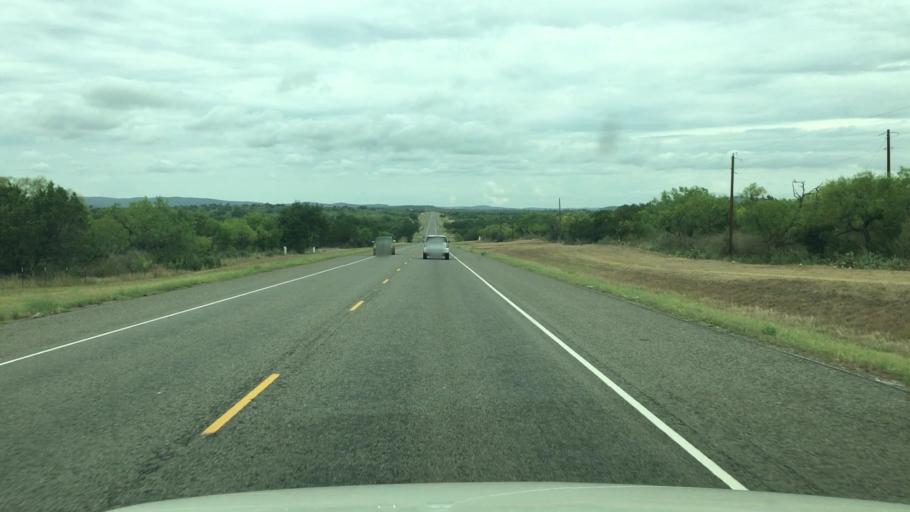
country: US
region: Texas
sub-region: Burnet County
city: Granite Shoals
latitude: 30.5522
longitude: -98.4660
